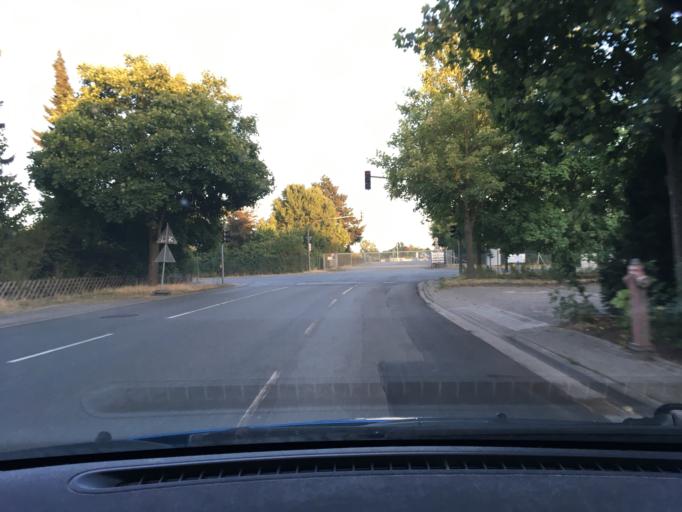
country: DE
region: Lower Saxony
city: Uelzen
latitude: 52.9812
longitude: 10.5605
